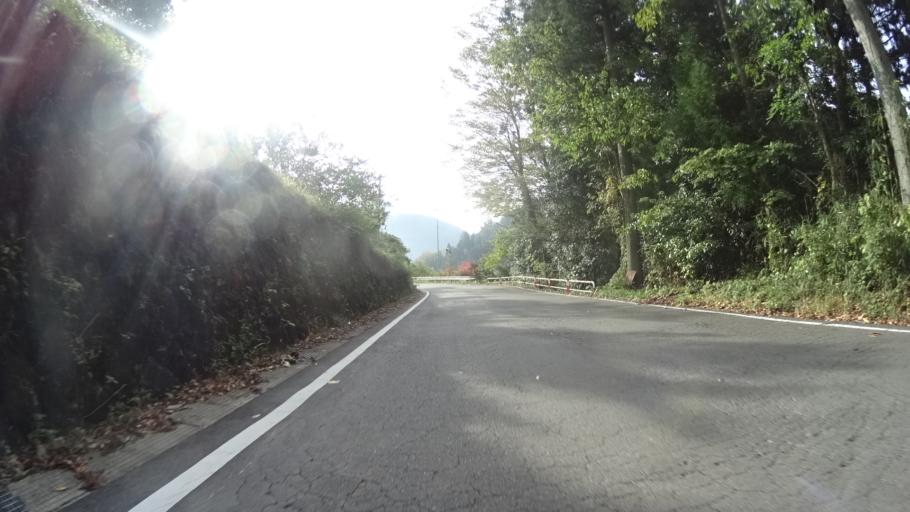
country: JP
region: Yamanashi
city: Uenohara
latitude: 35.6760
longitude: 139.0872
